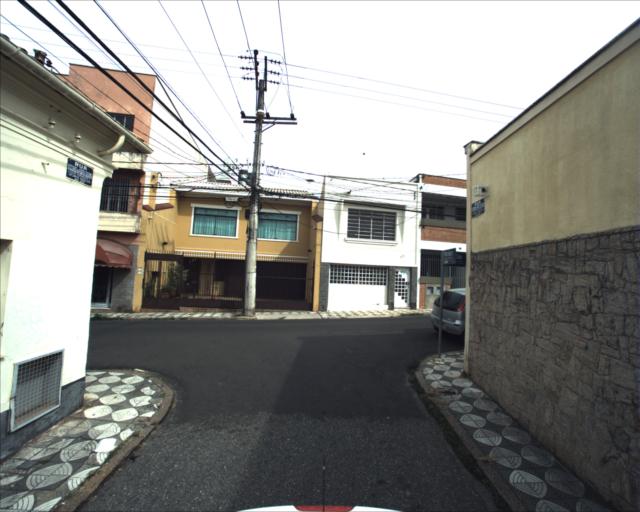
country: BR
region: Sao Paulo
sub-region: Sorocaba
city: Sorocaba
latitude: -23.5035
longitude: -47.4580
